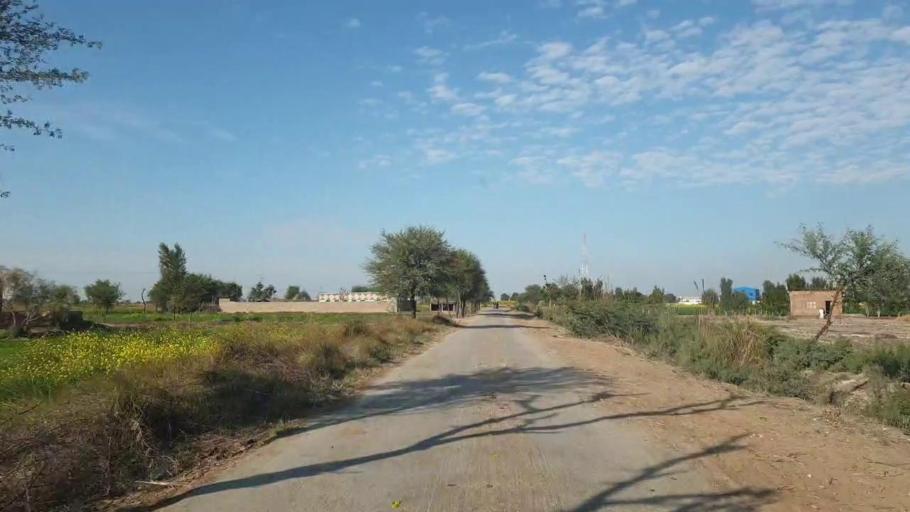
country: PK
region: Sindh
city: Sanghar
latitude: 26.0837
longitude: 68.8764
